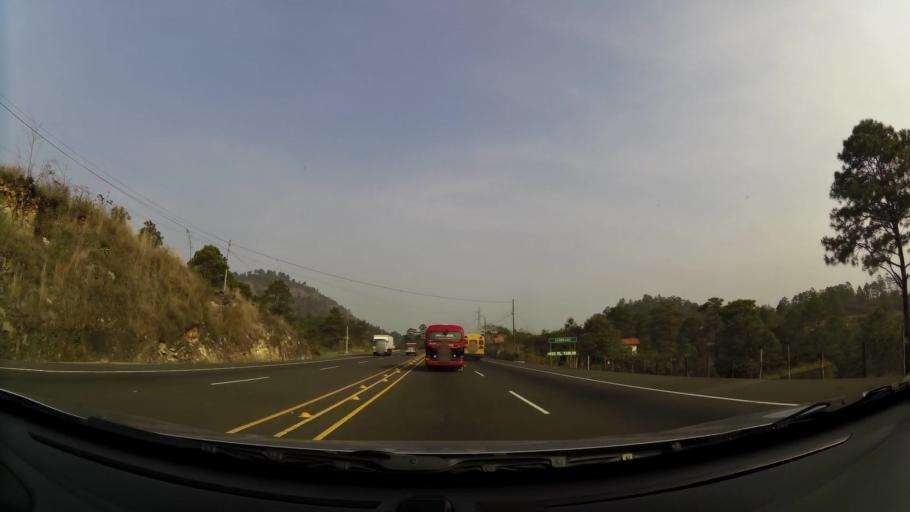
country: HN
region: Francisco Morazan
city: Zambrano
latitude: 14.2648
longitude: -87.3941
